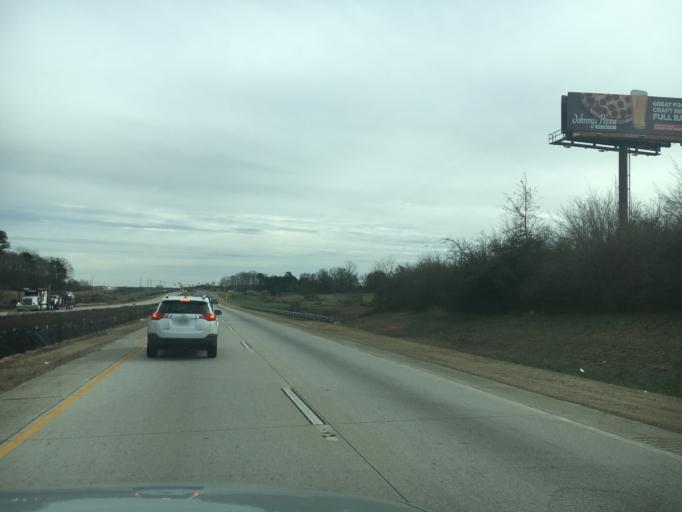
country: US
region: Georgia
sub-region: Barrow County
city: Winder
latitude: 33.9489
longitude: -83.7593
